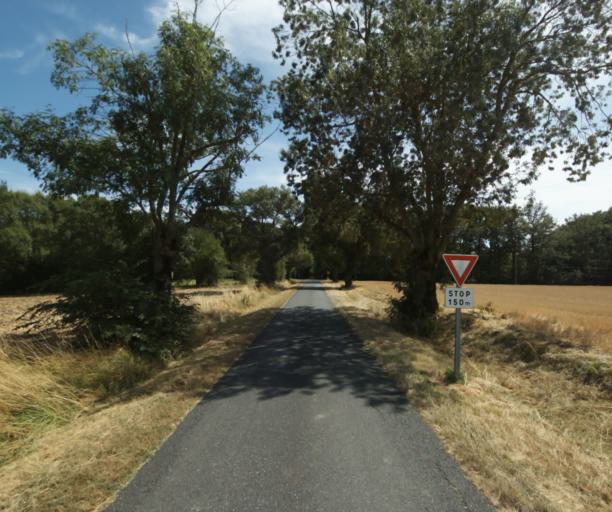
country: FR
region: Midi-Pyrenees
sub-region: Departement du Tarn
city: Puylaurens
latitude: 43.5267
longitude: 2.0234
